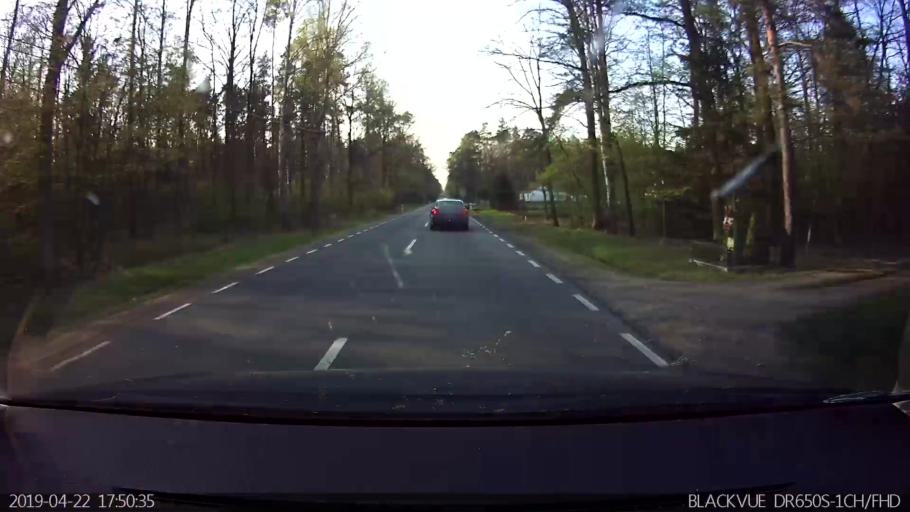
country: PL
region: Masovian Voivodeship
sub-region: Powiat wegrowski
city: Wegrow
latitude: 52.4264
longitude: 22.0007
